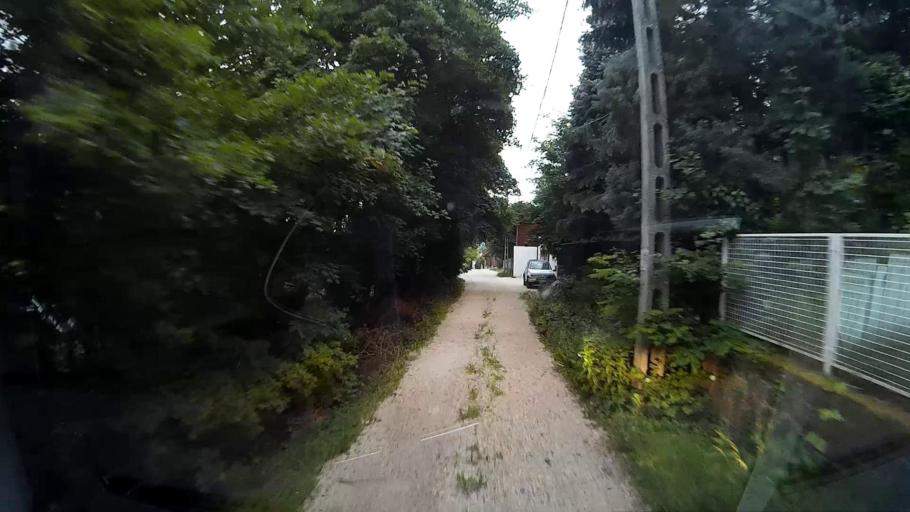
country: HU
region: Pest
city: Leanyfalu
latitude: 47.7131
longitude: 19.0805
